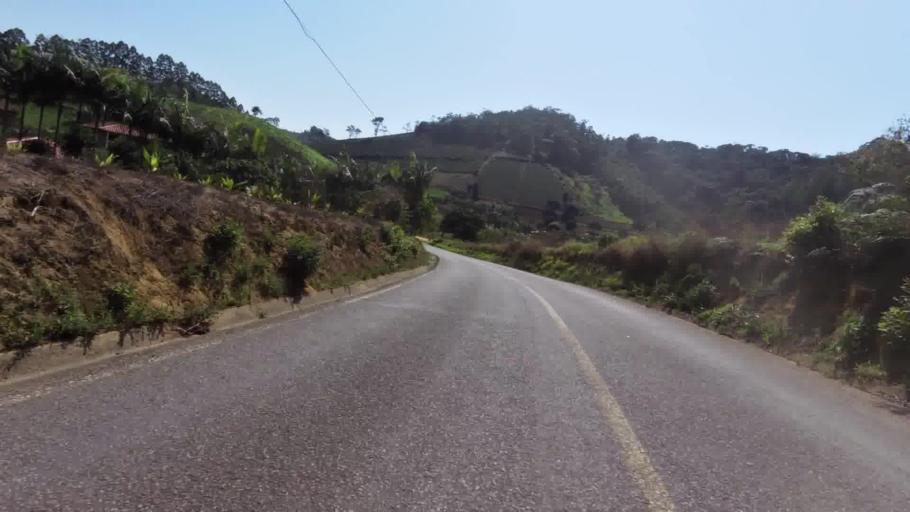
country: BR
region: Espirito Santo
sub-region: Marechal Floriano
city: Marechal Floriano
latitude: -20.4282
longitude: -40.8743
